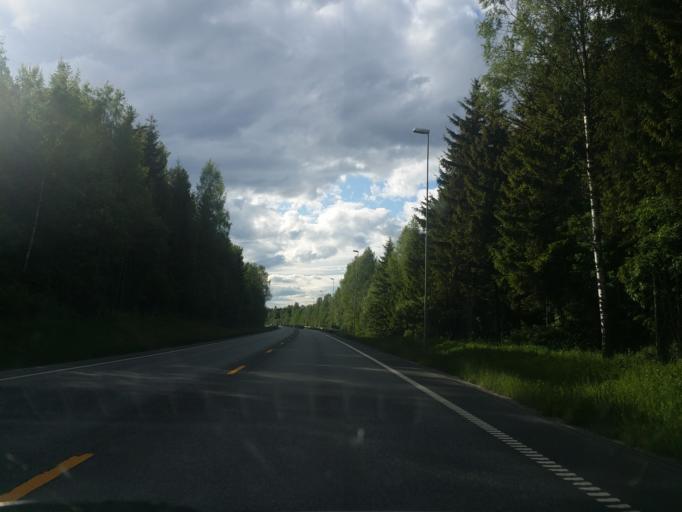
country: NO
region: Hedmark
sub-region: Stange
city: Stange
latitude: 60.7643
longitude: 11.1833
